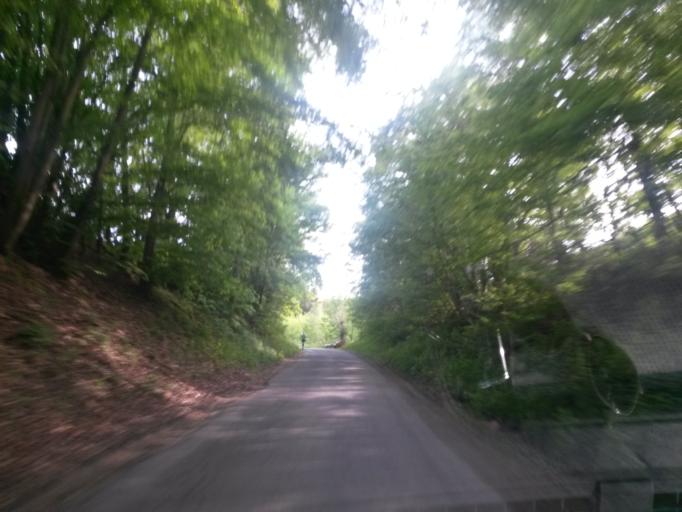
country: DE
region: North Rhine-Westphalia
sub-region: Regierungsbezirk Arnsberg
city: Nachrodt-Wiblingwerde
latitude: 51.3046
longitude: 7.5551
